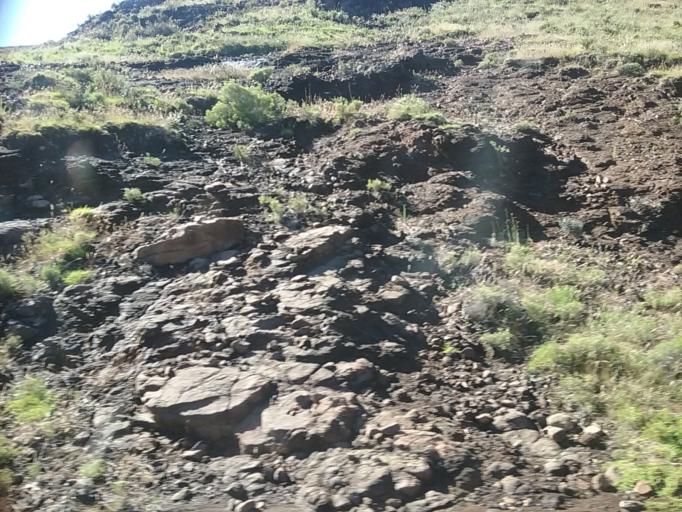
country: LS
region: Berea
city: Teyateyaneng
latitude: -29.2324
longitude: 27.9246
